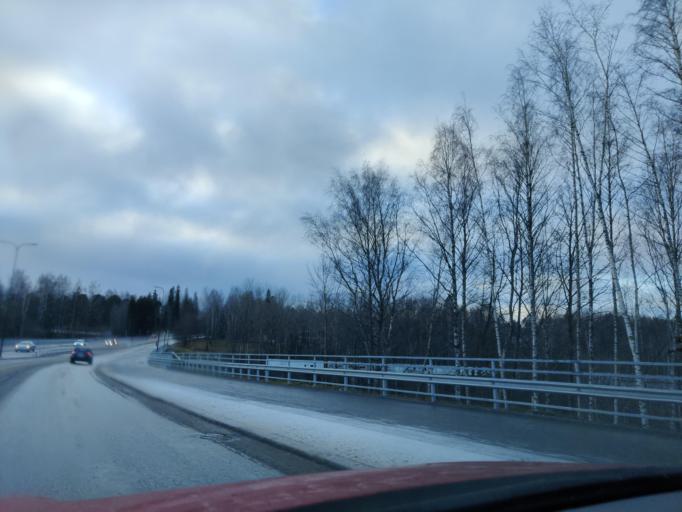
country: FI
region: Pirkanmaa
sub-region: Tampere
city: Nokia
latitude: 61.4739
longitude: 23.5055
